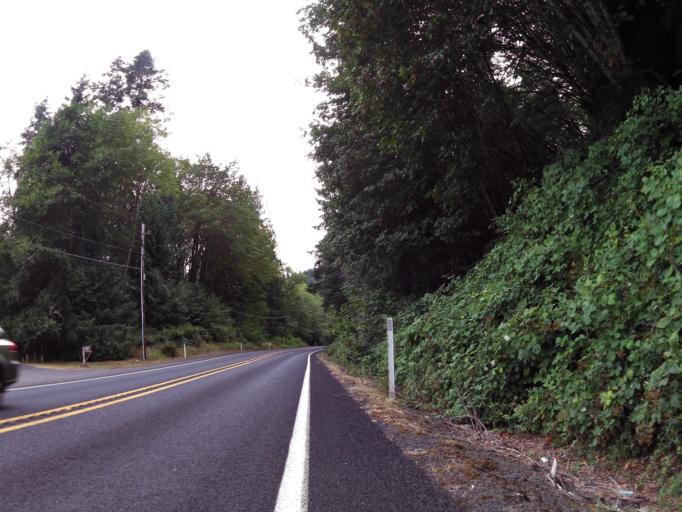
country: US
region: Oregon
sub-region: Columbia County
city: Clatskanie
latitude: 46.1736
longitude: -123.2280
